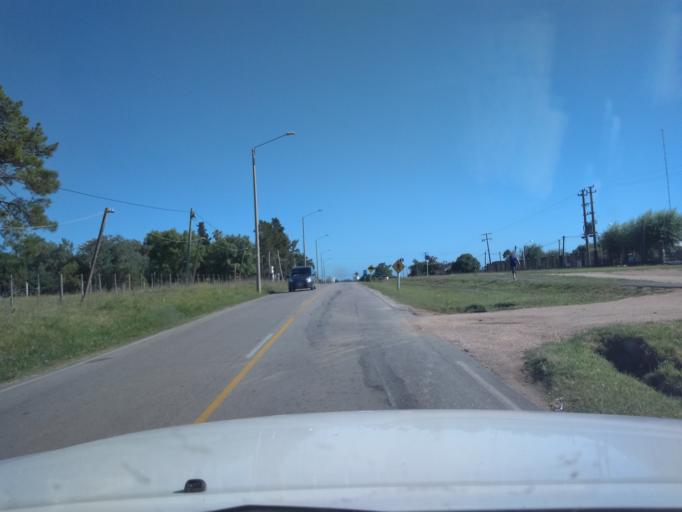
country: UY
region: Canelones
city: San Ramon
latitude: -34.3054
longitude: -55.9583
